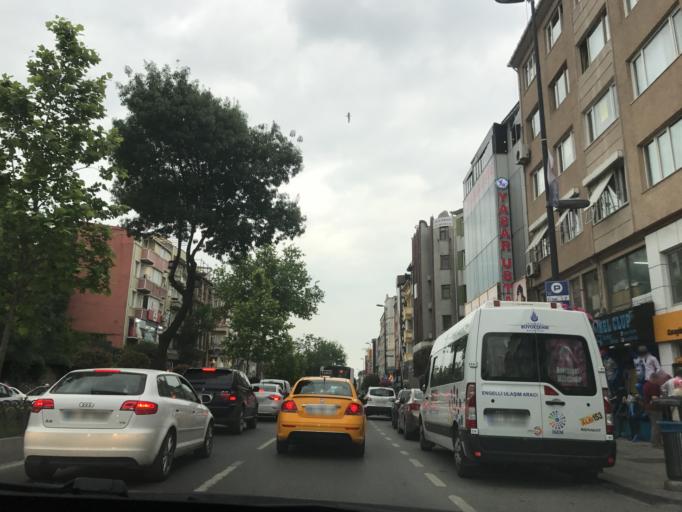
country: TR
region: Istanbul
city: Istanbul
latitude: 41.0247
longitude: 28.9412
